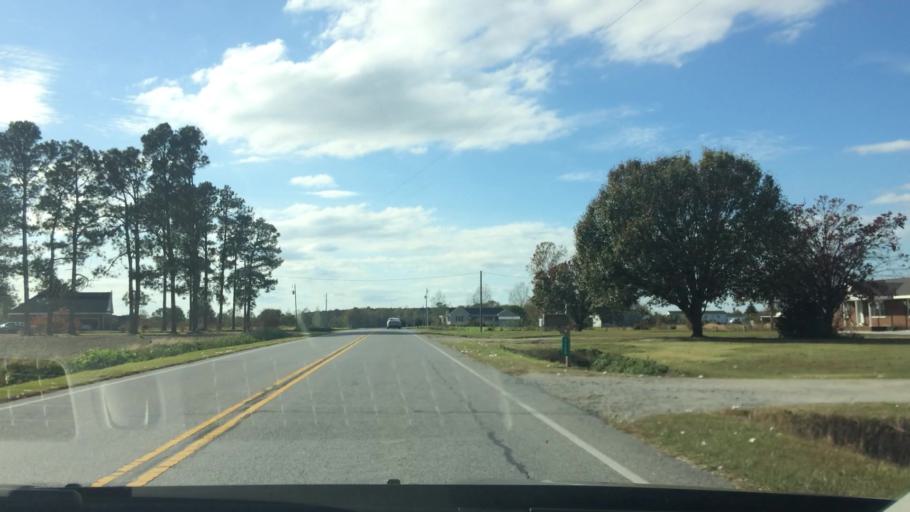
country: US
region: North Carolina
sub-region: Greene County
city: Snow Hill
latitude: 35.4419
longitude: -77.8072
